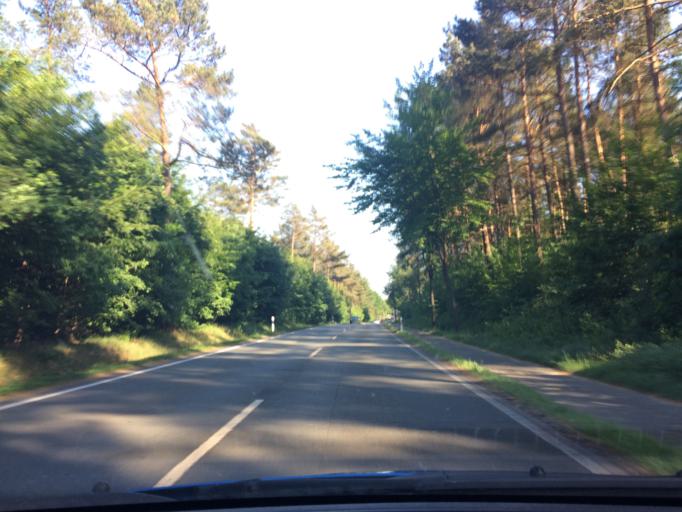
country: DE
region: Lower Saxony
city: Soltau
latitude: 53.0186
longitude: 9.8791
